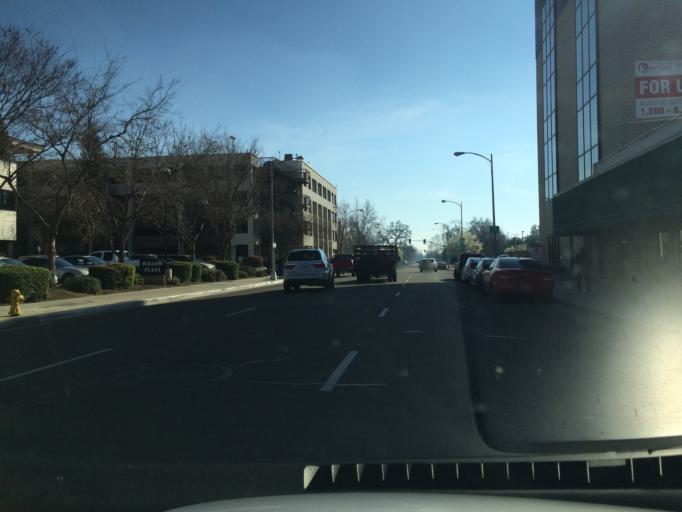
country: US
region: California
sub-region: Tulare County
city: Visalia
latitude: 36.3290
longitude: -119.2934
